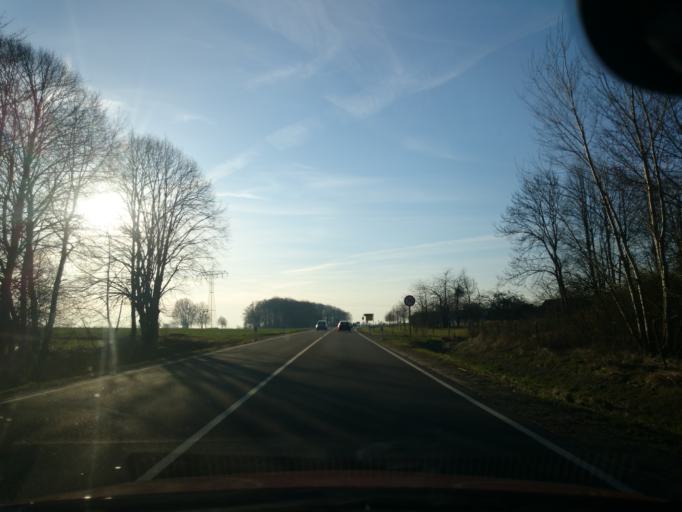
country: DE
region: Mecklenburg-Vorpommern
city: Brandshagen
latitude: 54.2358
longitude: 13.1700
